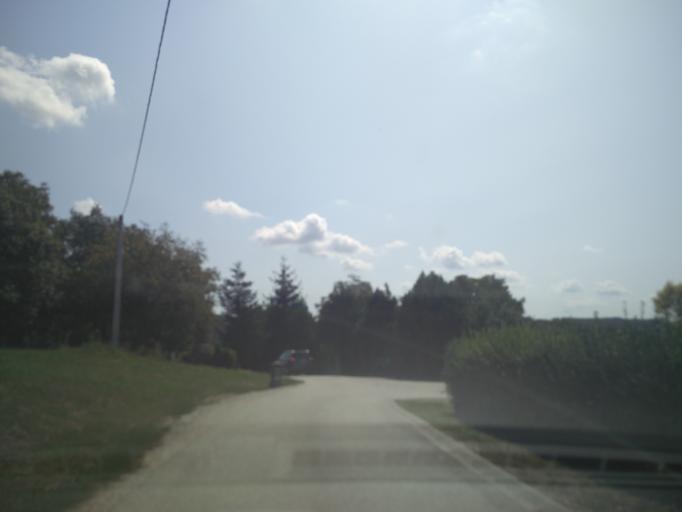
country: HU
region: Zala
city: Zalaegerszeg
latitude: 46.8378
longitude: 16.8895
